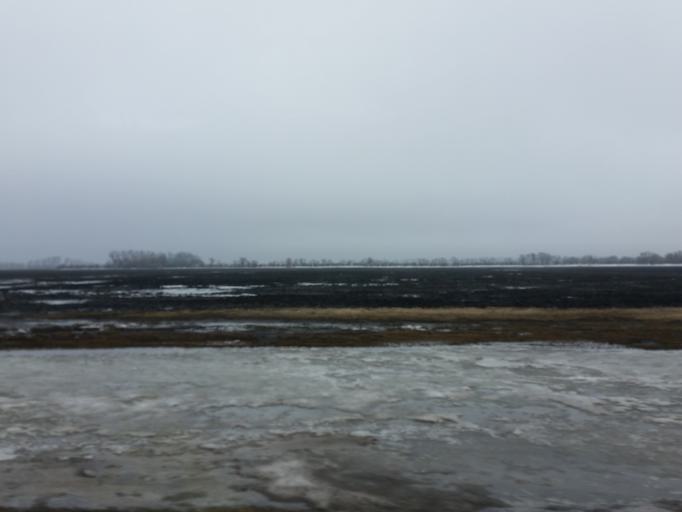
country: US
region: North Dakota
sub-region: Walsh County
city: Grafton
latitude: 48.5718
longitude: -97.3591
